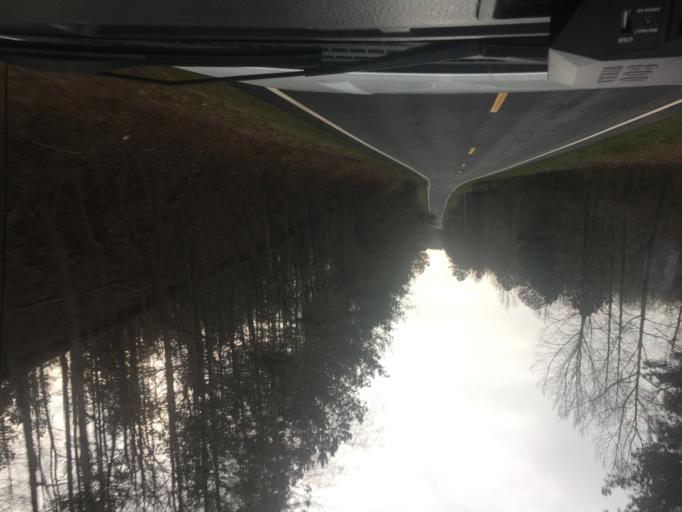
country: US
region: Georgia
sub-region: Dawson County
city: Dawsonville
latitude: 34.3520
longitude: -84.2063
